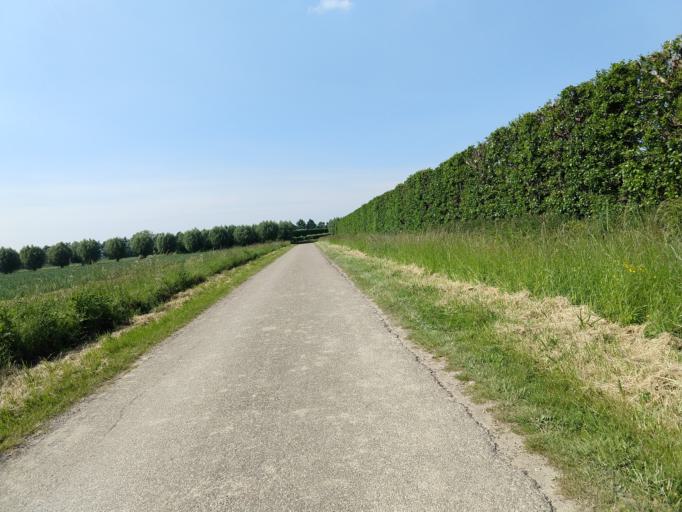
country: NL
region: Zeeland
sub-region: Gemeente Goes
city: Goes
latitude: 51.4412
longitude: 3.8593
